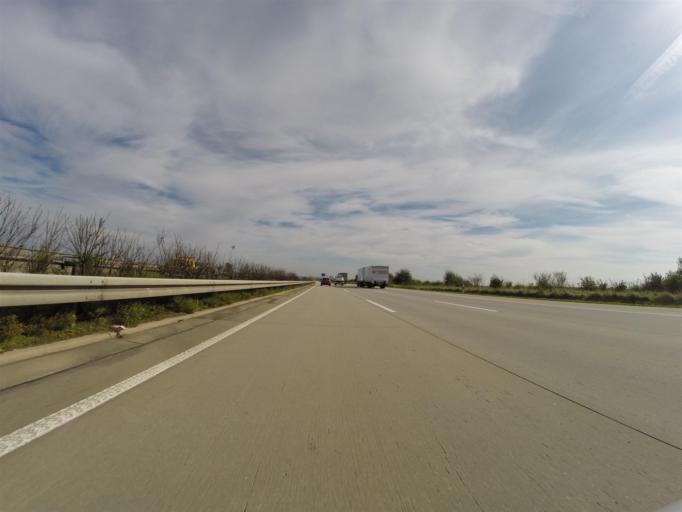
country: DE
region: Thuringia
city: Kraftsdorf
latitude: 50.8909
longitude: 11.9562
